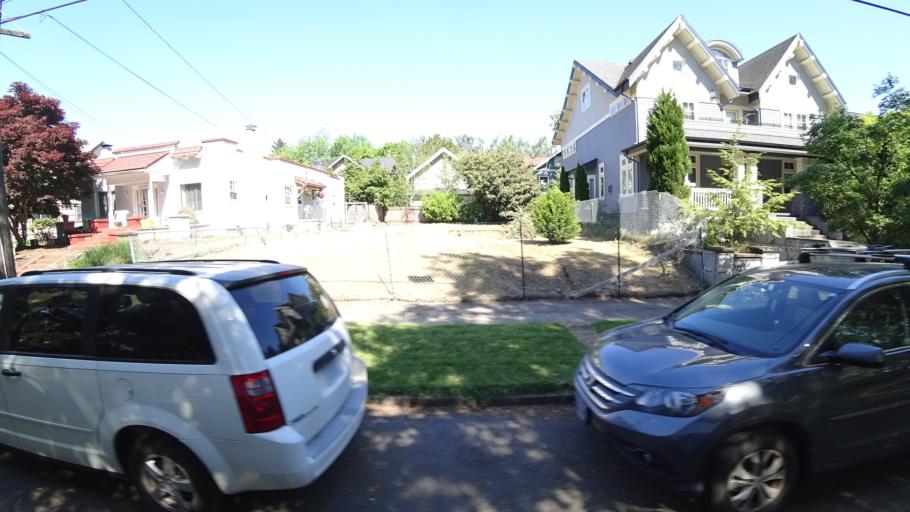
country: US
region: Oregon
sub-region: Multnomah County
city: Portland
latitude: 45.5413
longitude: -122.6525
